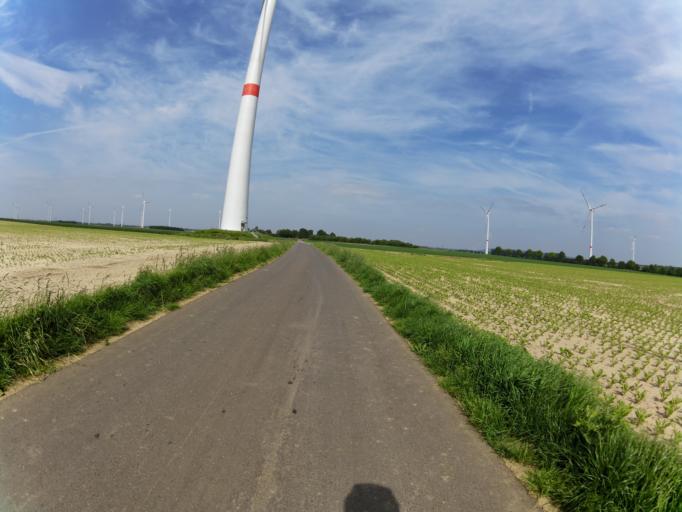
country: DE
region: North Rhine-Westphalia
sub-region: Regierungsbezirk Koln
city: Aldenhoven
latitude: 50.9131
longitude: 6.2698
